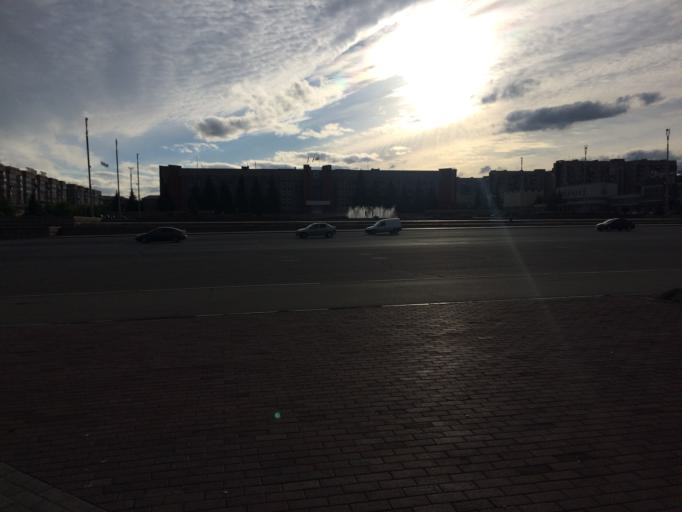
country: RU
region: Chelyabinsk
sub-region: Gorod Magnitogorsk
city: Magnitogorsk
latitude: 53.4069
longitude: 58.9863
